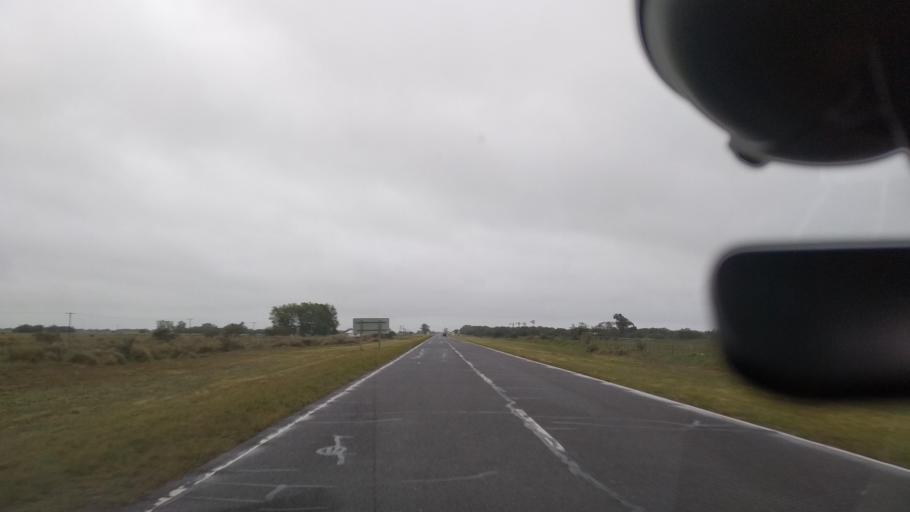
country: AR
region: Buenos Aires
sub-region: Partido de Dolores
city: Dolores
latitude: -36.0425
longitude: -57.4456
